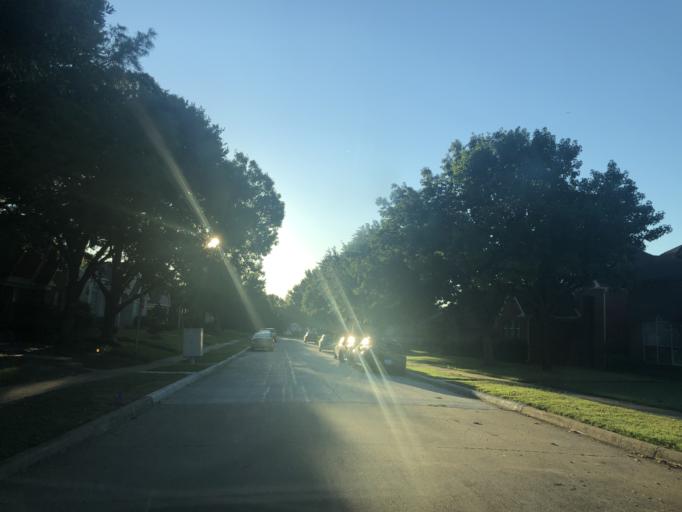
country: US
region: Texas
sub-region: Dallas County
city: Grand Prairie
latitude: 32.6660
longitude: -96.9935
